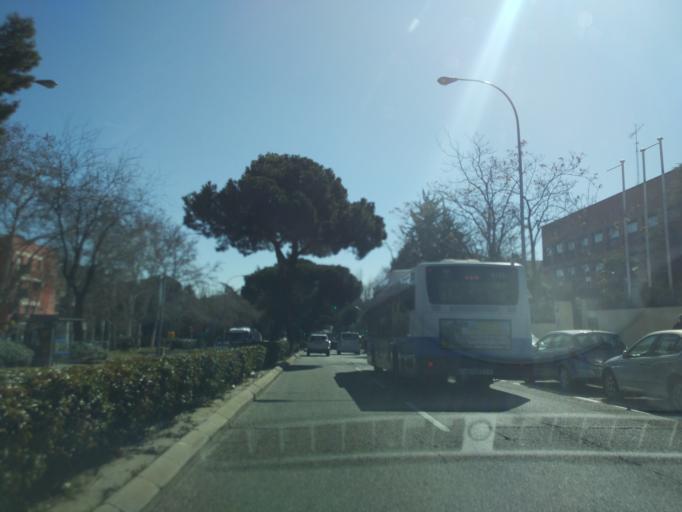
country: ES
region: Madrid
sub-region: Provincia de Madrid
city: Ciudad Lineal
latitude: 40.4549
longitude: -3.6557
